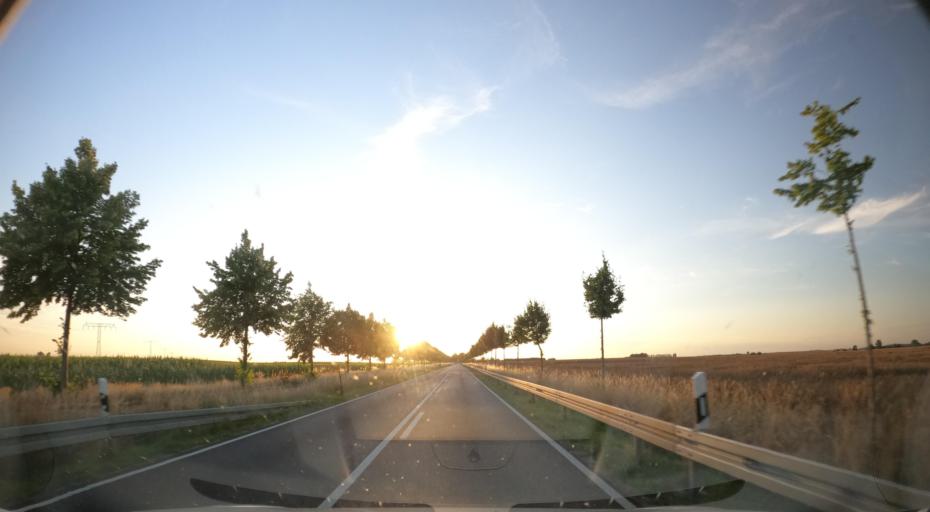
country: DE
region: Mecklenburg-Vorpommern
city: Strasburg
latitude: 53.4941
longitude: 13.7926
